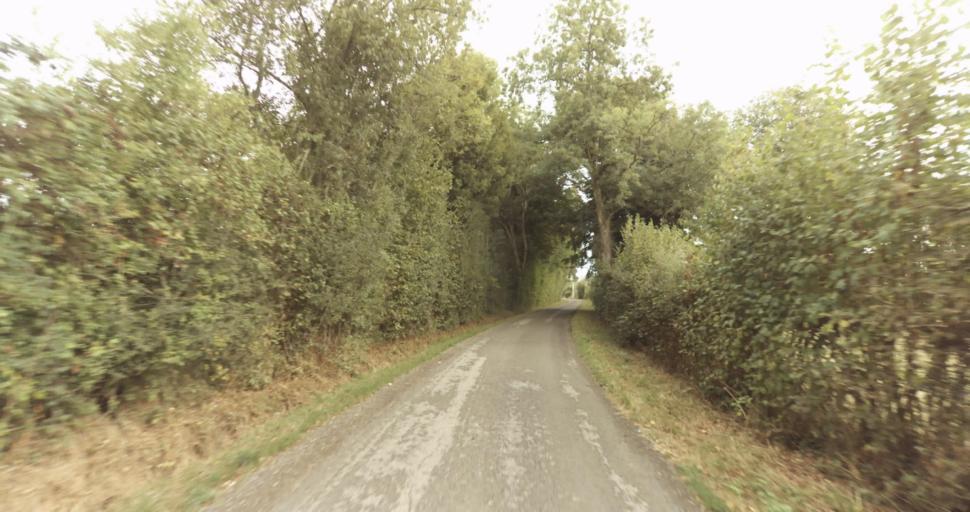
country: FR
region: Lower Normandy
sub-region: Departement de l'Orne
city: Sainte-Gauburge-Sainte-Colombe
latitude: 48.7199
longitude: 0.4765
